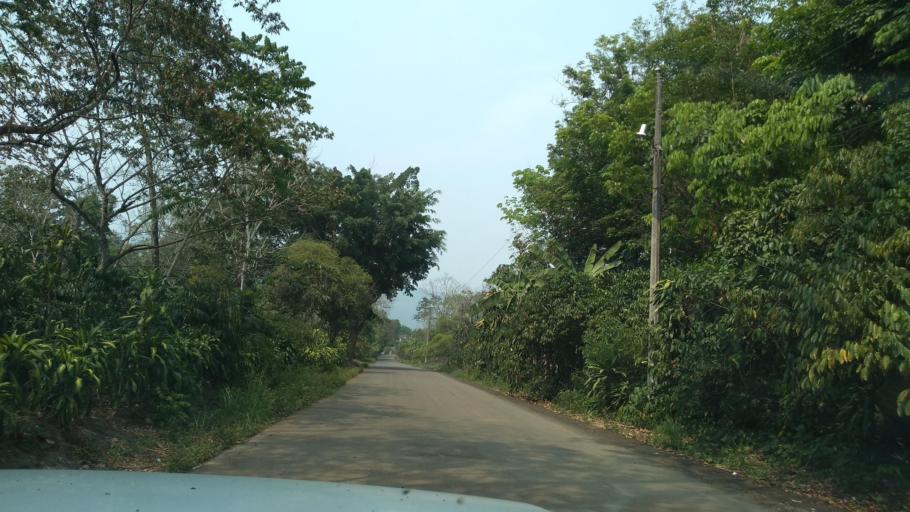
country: MX
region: Veracruz
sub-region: Tezonapa
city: Laguna Chica (Pueblo Nuevo)
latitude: 18.5383
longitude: -96.7837
